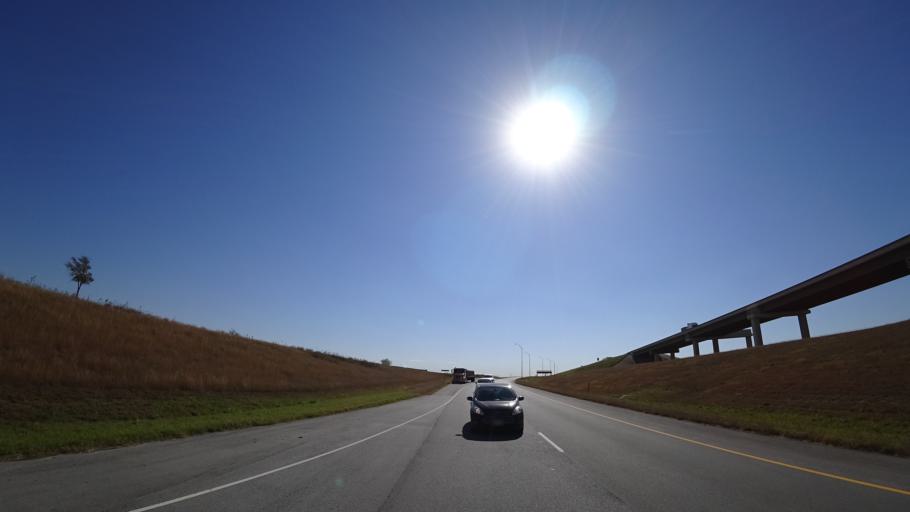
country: US
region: Texas
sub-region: Williamson County
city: Hutto
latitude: 30.5352
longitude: -97.5753
